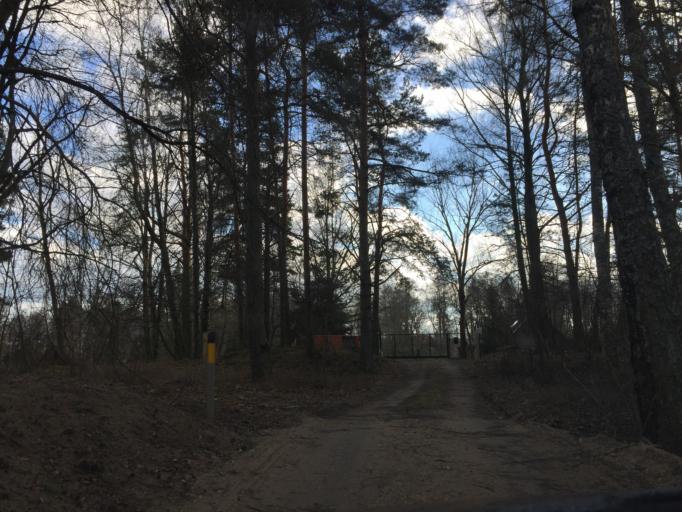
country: LV
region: Adazi
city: Adazi
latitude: 57.0573
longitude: 24.3385
